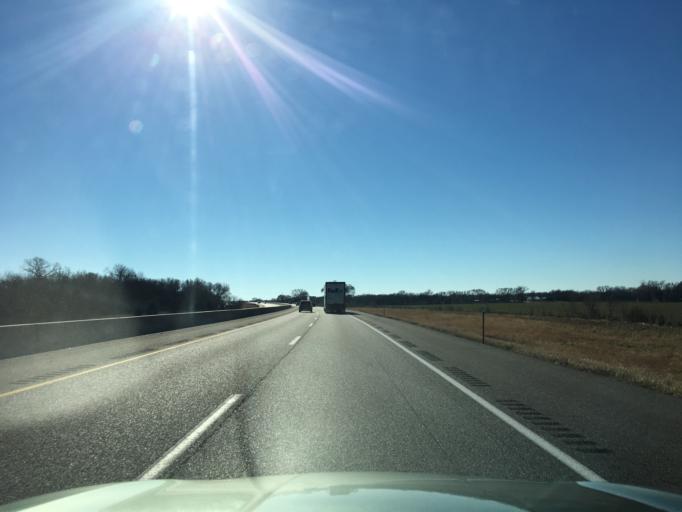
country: US
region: Kansas
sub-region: Sumner County
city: Belle Plaine
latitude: 37.3984
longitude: -97.3260
